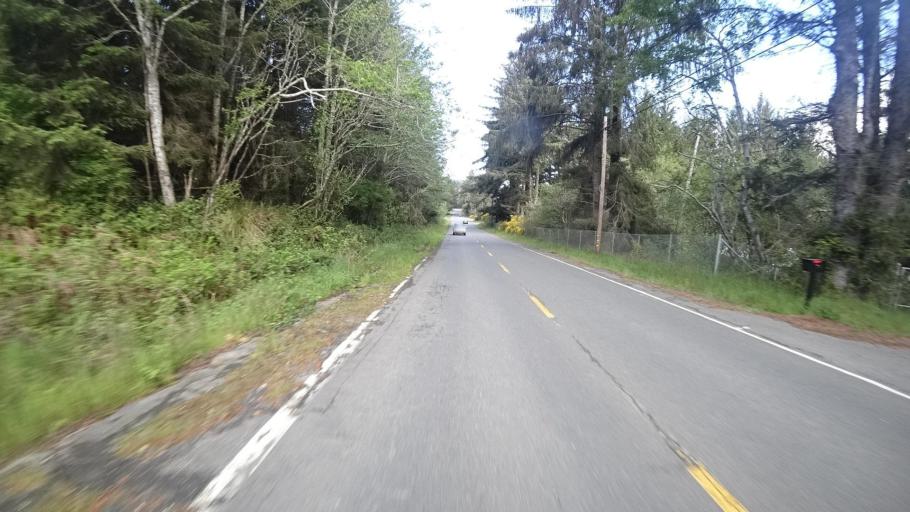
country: US
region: California
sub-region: Humboldt County
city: McKinleyville
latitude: 40.9845
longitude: -124.1047
